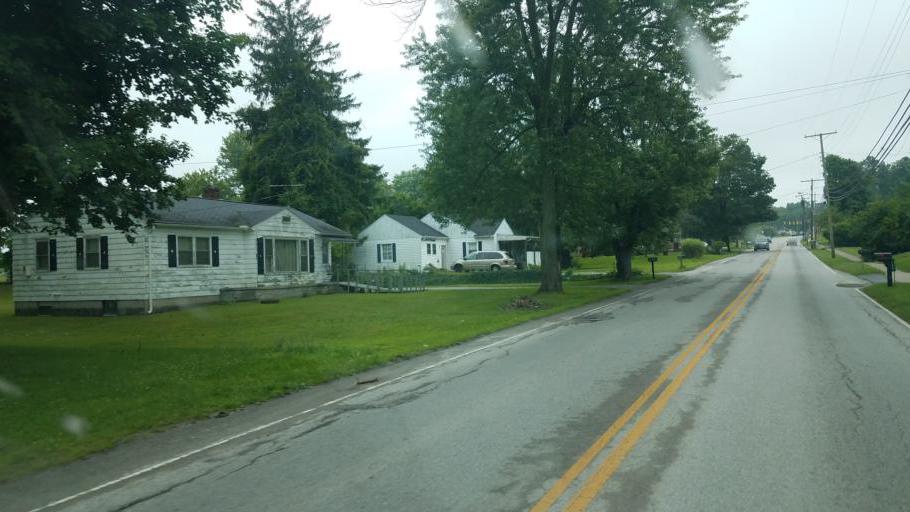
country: US
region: Ohio
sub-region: Highland County
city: Hillsboro
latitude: 39.2157
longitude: -83.6084
